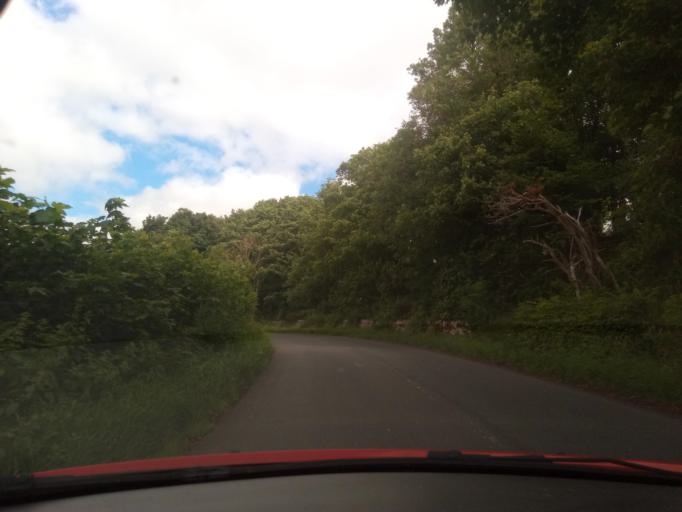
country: GB
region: Scotland
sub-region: The Scottish Borders
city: Kelso
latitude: 55.5292
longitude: -2.3570
